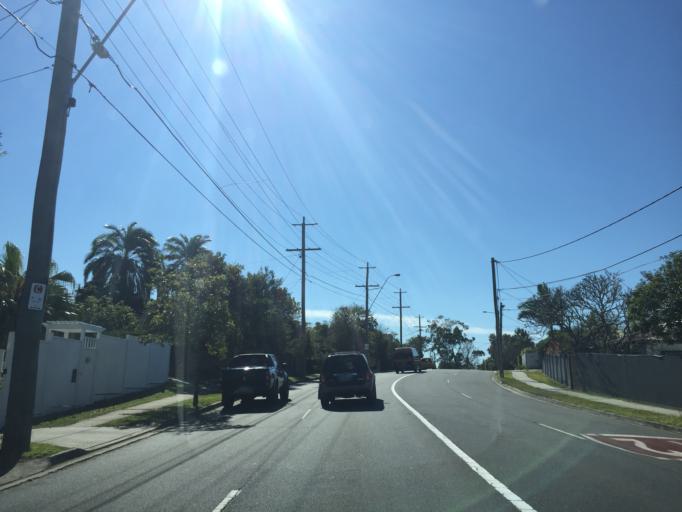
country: AU
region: Queensland
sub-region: Brisbane
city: Milton
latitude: -27.4475
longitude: 152.9828
